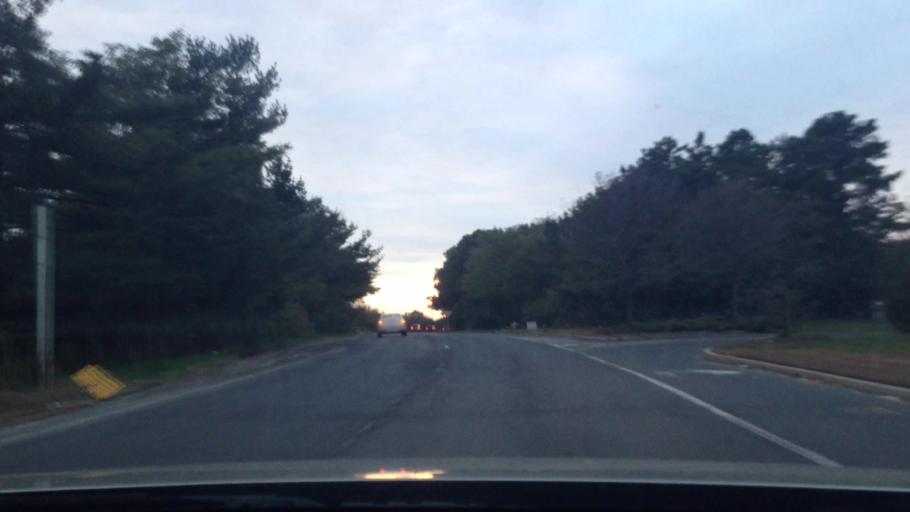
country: US
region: New York
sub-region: Suffolk County
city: Medford
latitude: 40.8246
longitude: -72.9966
